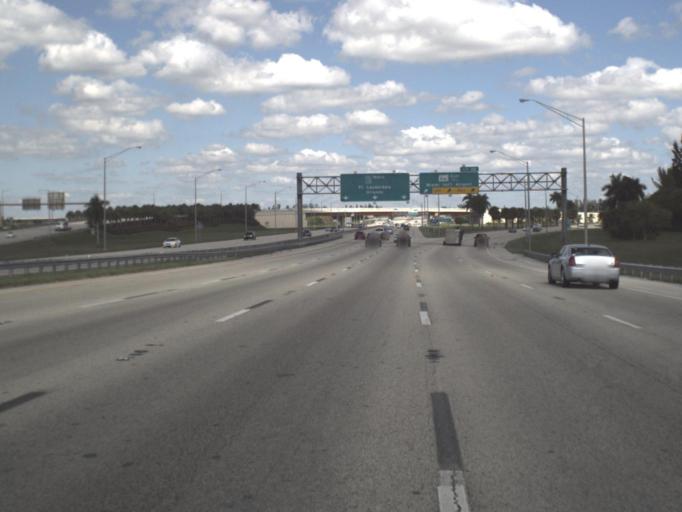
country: US
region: Florida
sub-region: Miami-Dade County
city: Sweetwater
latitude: 25.7705
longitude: -80.3856
